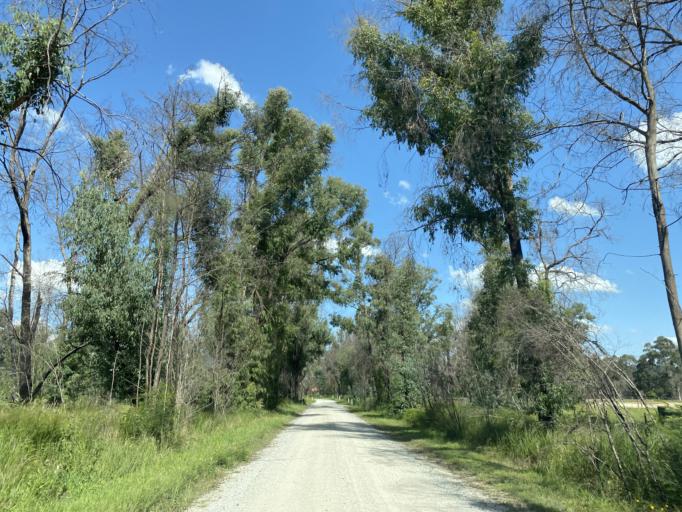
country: AU
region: Victoria
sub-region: Cardinia
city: Bunyip
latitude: -38.0076
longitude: 145.7423
